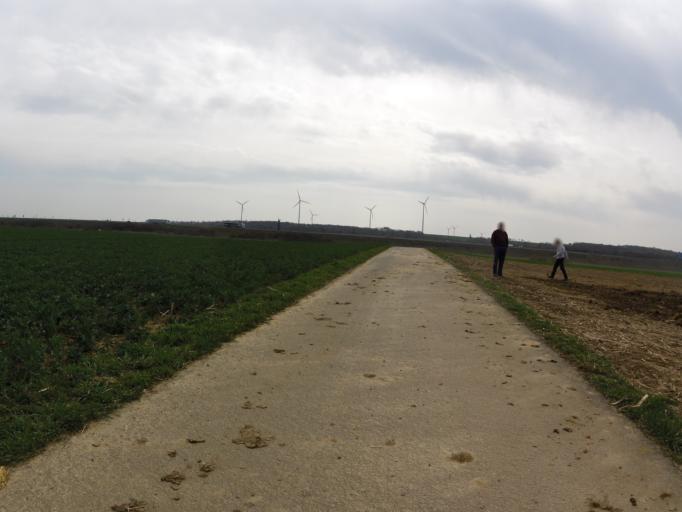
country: DE
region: Bavaria
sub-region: Regierungsbezirk Unterfranken
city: Biebelried
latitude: 49.7856
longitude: 10.1031
